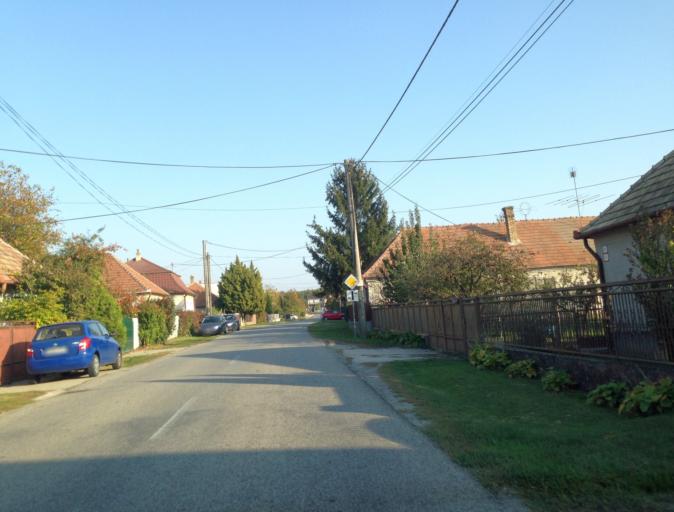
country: SK
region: Nitriansky
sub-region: Okres Komarno
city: Hurbanovo
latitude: 47.8894
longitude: 18.2030
